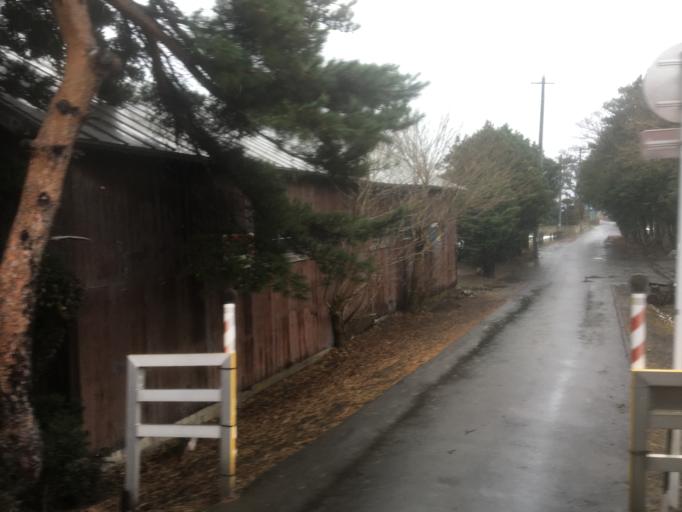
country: JP
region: Aomori
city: Aomori Shi
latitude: 40.9168
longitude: 140.6661
